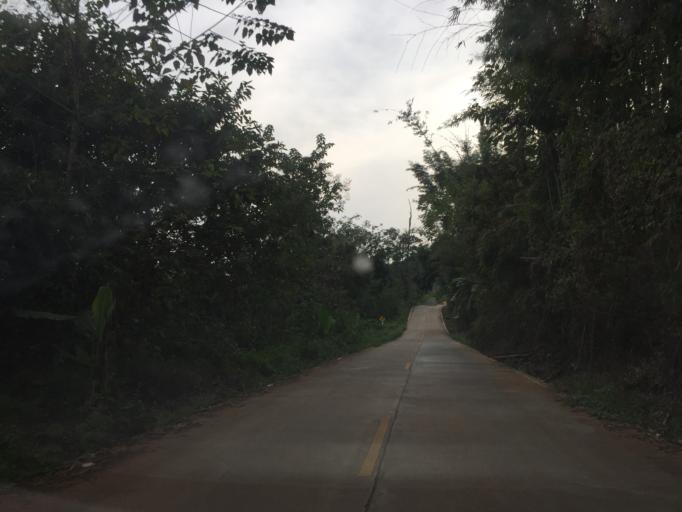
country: TH
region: Chiang Mai
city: Samoeng
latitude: 18.9682
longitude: 98.7181
